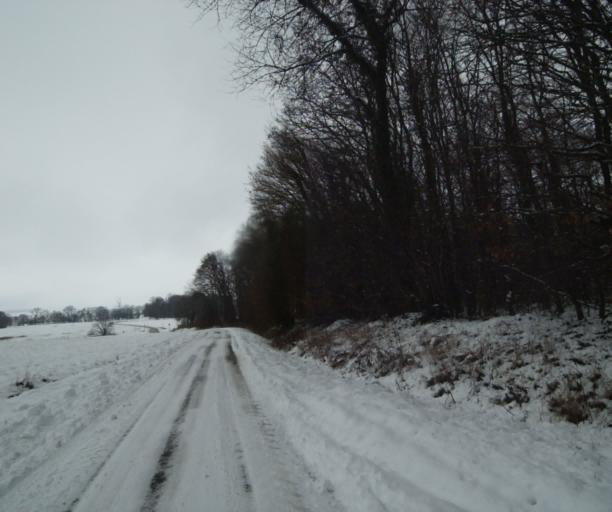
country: FR
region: Champagne-Ardenne
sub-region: Departement de la Haute-Marne
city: Wassy
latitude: 48.4523
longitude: 4.9467
